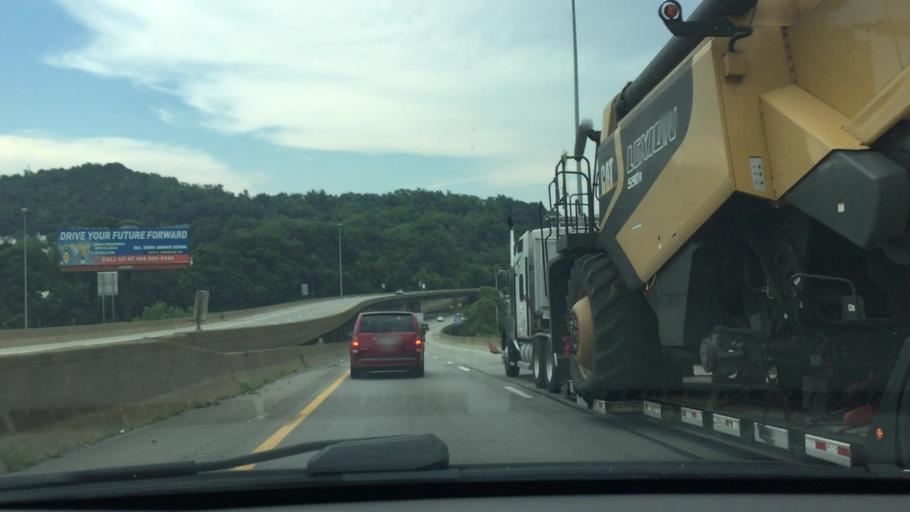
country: US
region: West Virginia
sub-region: Ohio County
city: Bethlehem
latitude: 40.0495
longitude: -80.6678
